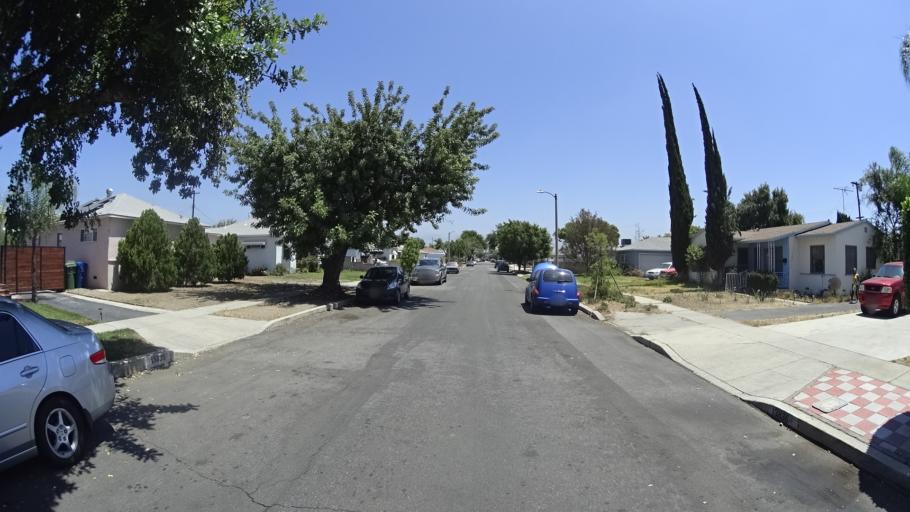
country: US
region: California
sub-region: Los Angeles County
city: San Fernando
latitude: 34.2339
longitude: -118.4349
